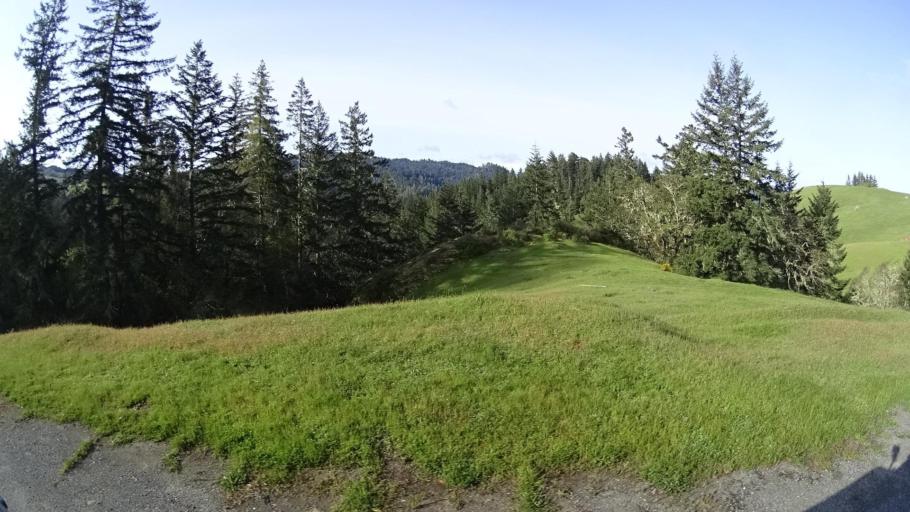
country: US
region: California
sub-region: Humboldt County
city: Hydesville
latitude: 40.6743
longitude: -123.9332
